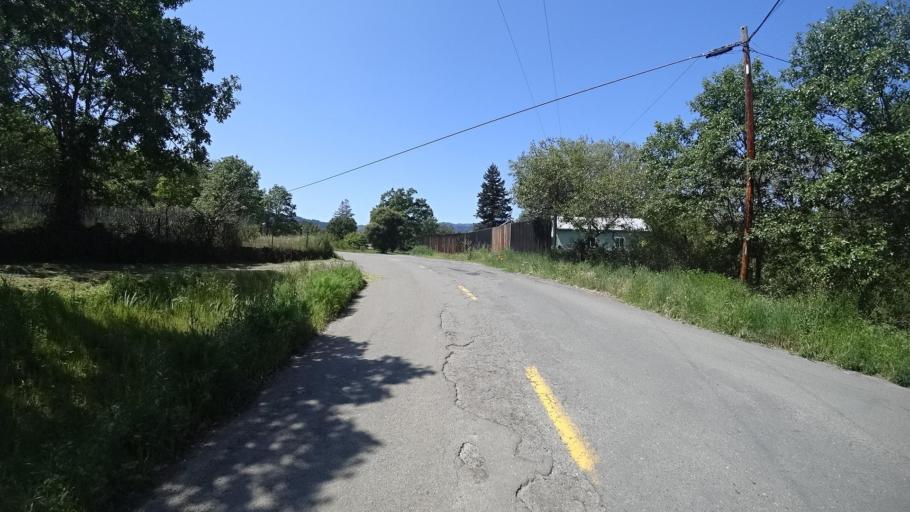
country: US
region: California
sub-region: Humboldt County
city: Redway
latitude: 40.1757
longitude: -123.6101
